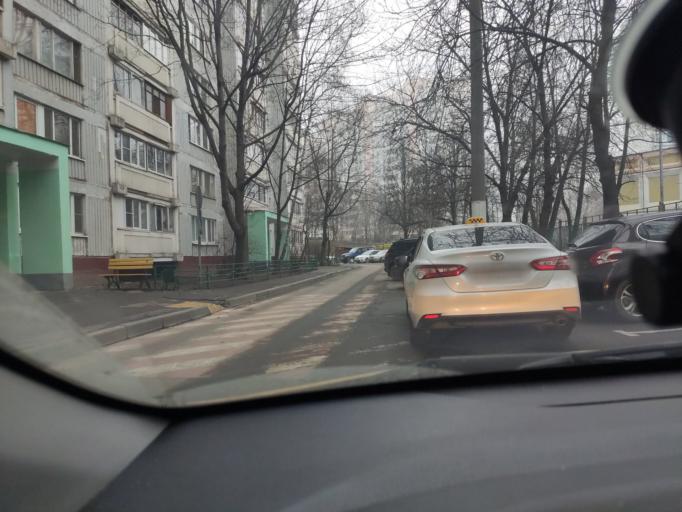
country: RU
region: Moscow
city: Chertanovo Yuzhnoye
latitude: 55.5891
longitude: 37.5949
